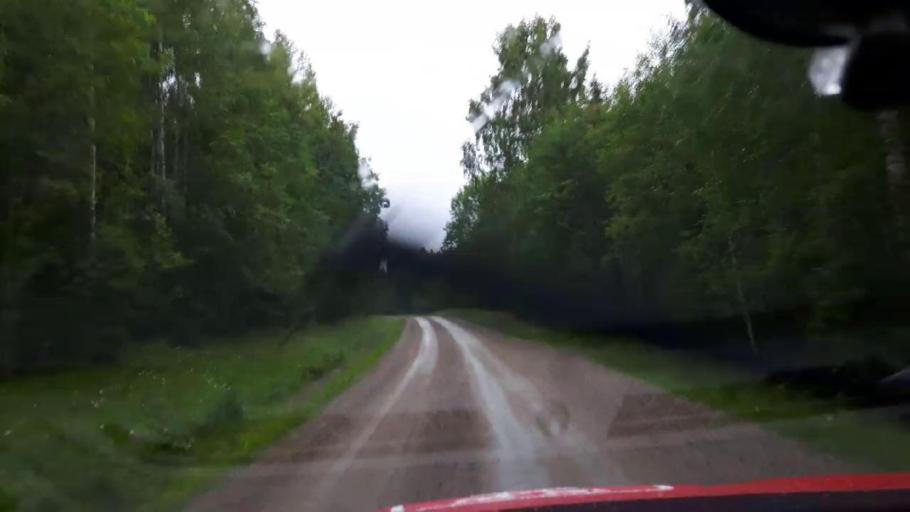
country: SE
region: Jaemtland
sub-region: OEstersunds Kommun
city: Brunflo
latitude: 62.7931
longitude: 14.9630
